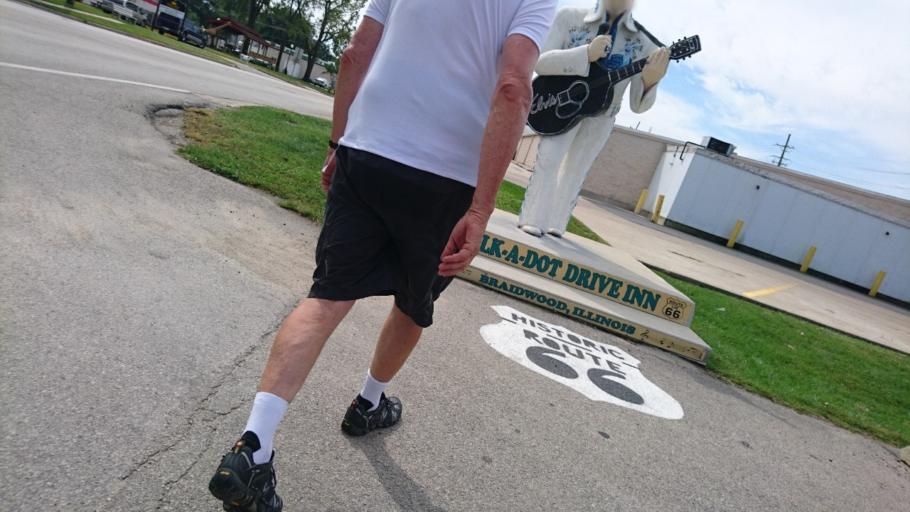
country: US
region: Illinois
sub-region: Will County
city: Braidwood
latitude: 41.2650
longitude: -88.2100
